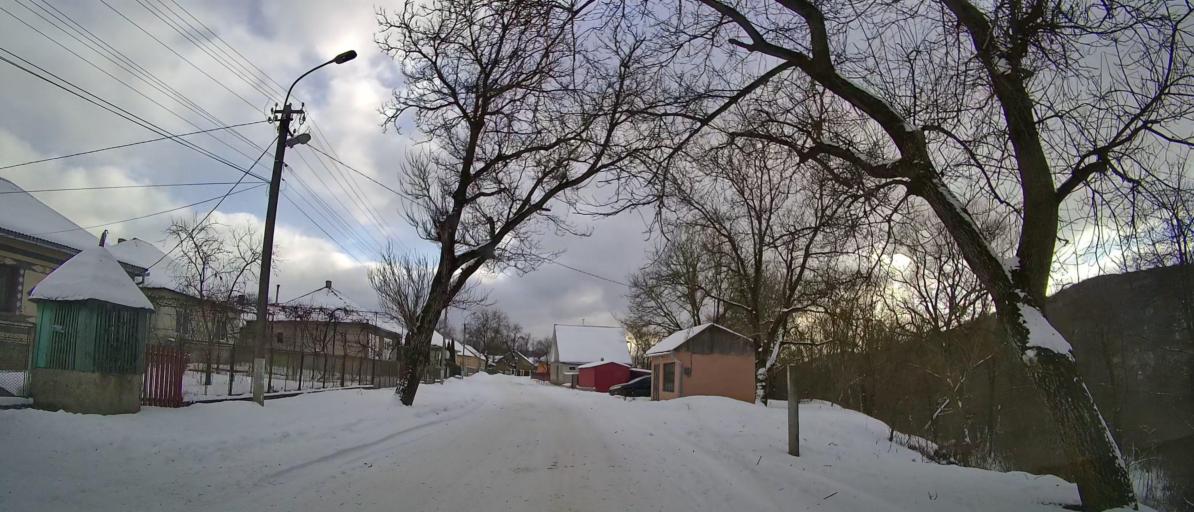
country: UA
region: Zakarpattia
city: Velykyi Bereznyi
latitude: 48.9209
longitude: 22.4639
